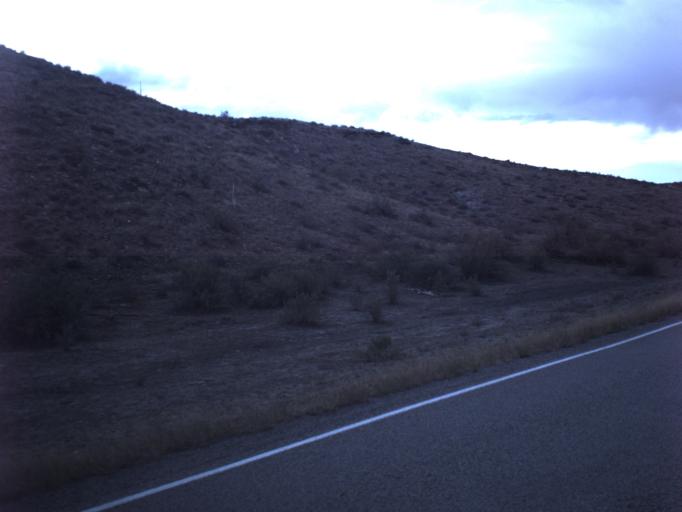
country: US
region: Utah
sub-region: Grand County
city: Moab
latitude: 38.8525
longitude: -109.2861
